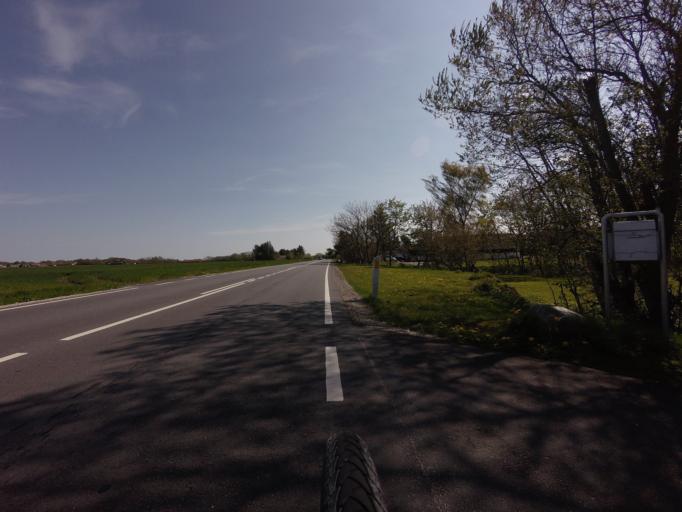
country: DK
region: North Denmark
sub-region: Jammerbugt Kommune
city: Pandrup
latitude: 57.2244
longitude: 9.6574
